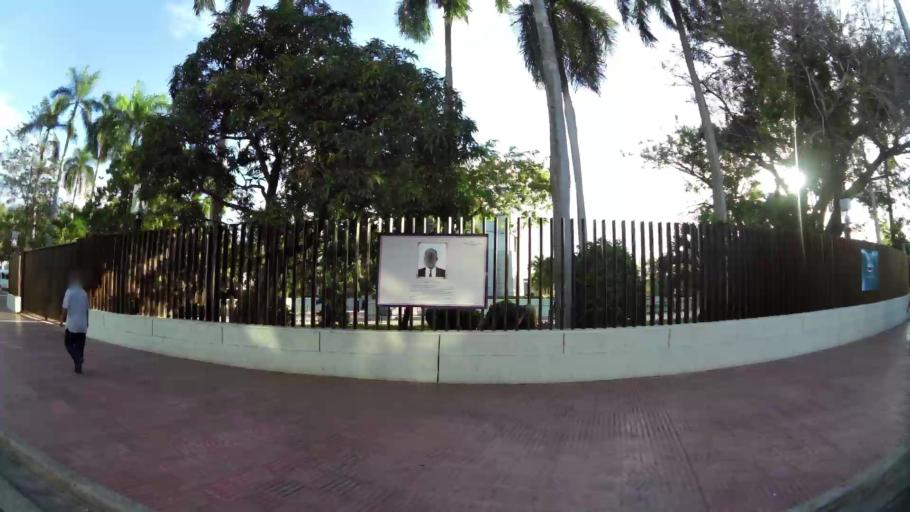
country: DO
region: Nacional
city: Ciudad Nueva
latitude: 18.4709
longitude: -69.8928
